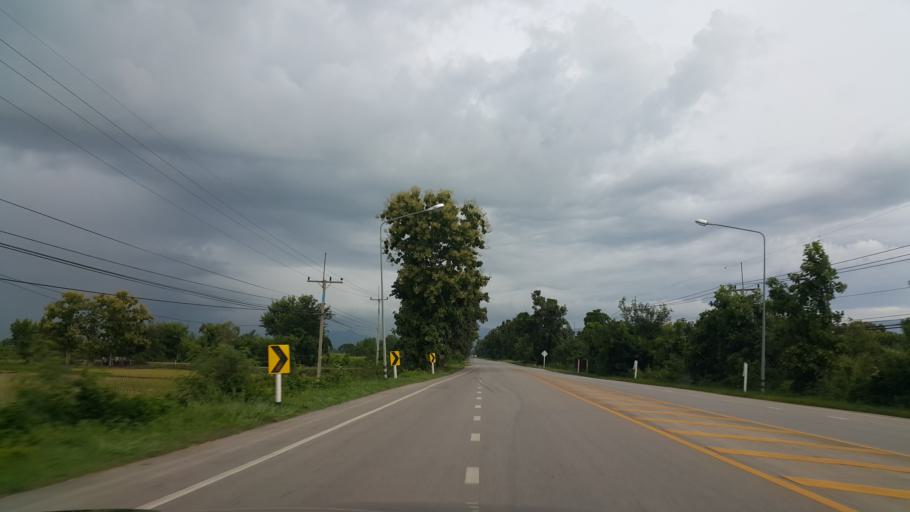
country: TH
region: Phayao
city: Dok Kham Tai
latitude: 19.1790
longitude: 100.0123
